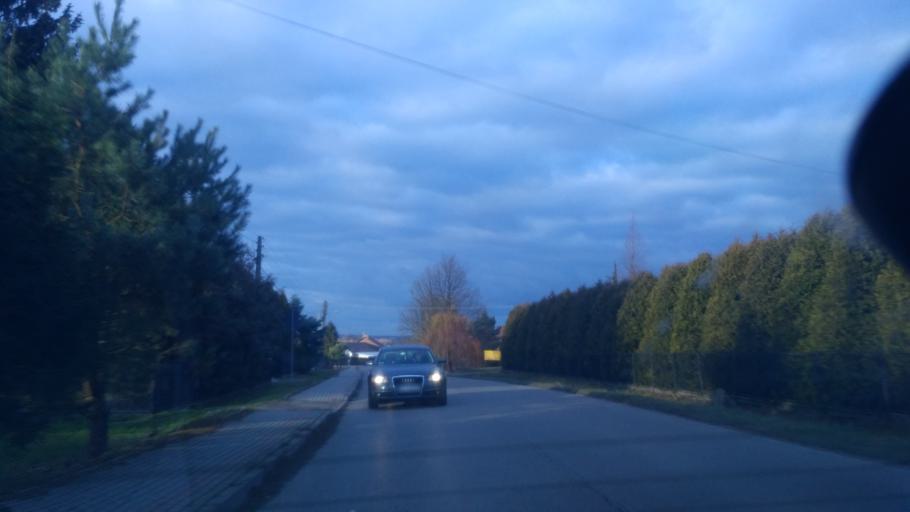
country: PL
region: Subcarpathian Voivodeship
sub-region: Powiat rzeszowski
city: Krasne
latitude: 50.0590
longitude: 22.1198
